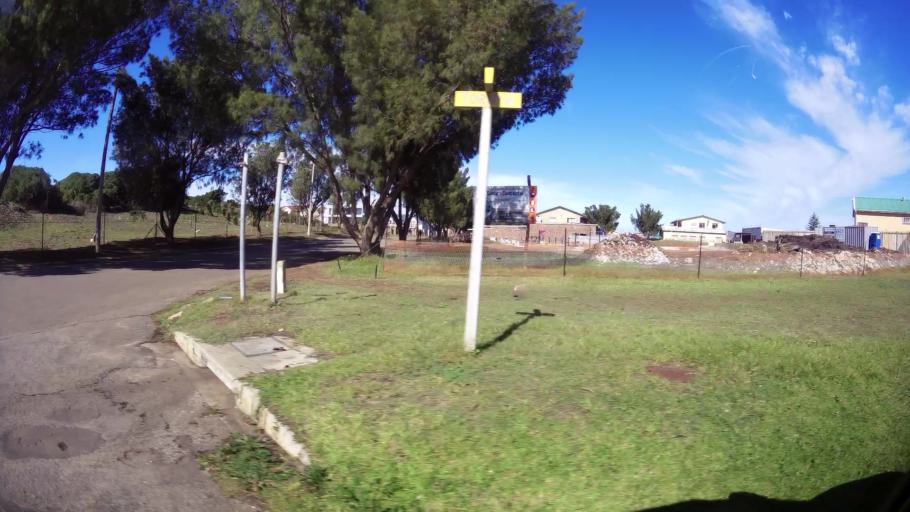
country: ZA
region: Eastern Cape
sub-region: Cacadu District Municipality
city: Jeffrey's Bay
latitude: -34.0586
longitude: 24.9230
